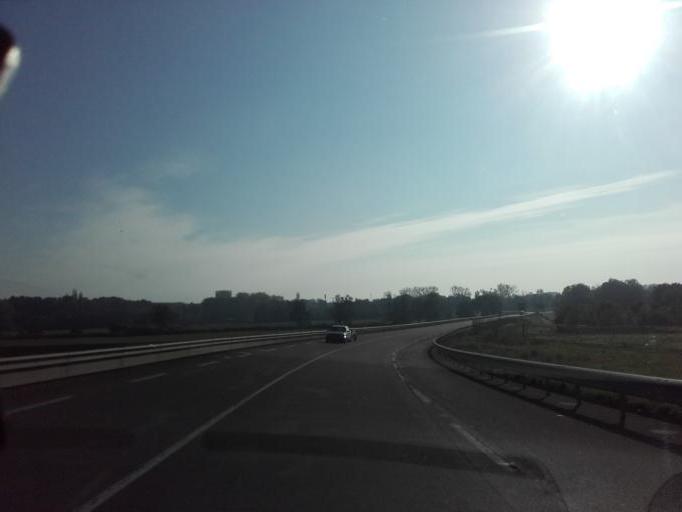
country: FR
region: Bourgogne
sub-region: Departement de Saone-et-Loire
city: Champforgeuil
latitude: 46.8087
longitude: 4.8302
